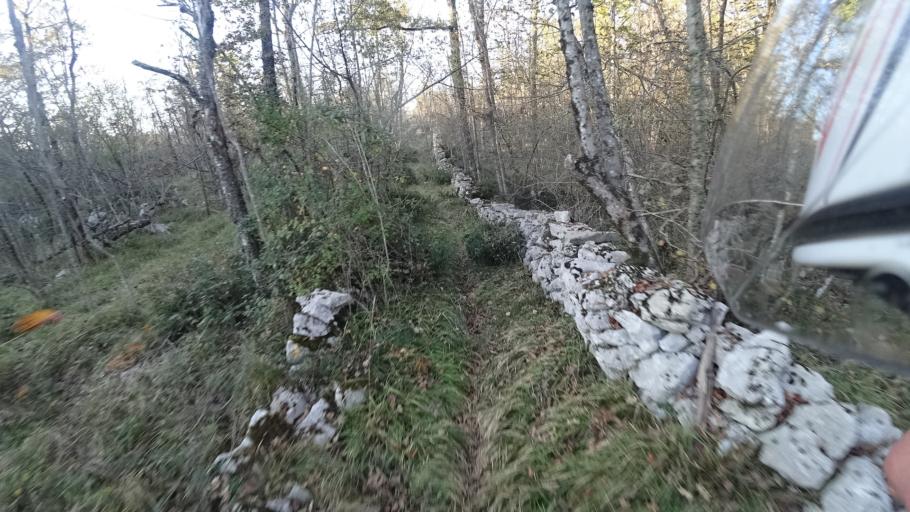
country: HR
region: Primorsko-Goranska
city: Kastav
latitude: 45.4035
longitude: 14.3170
